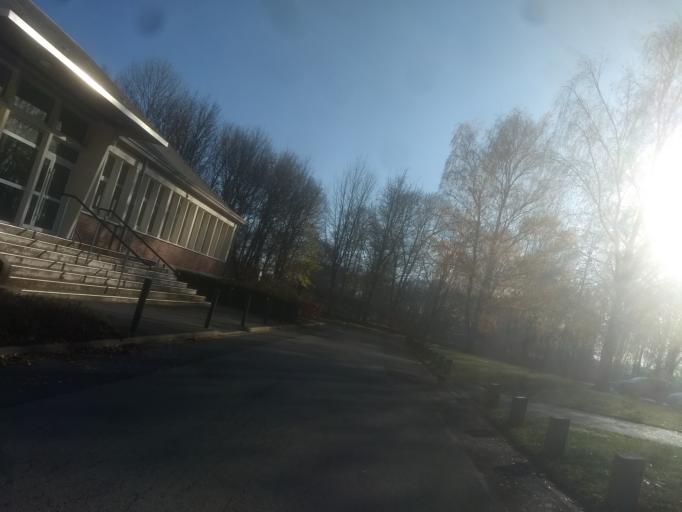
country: FR
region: Nord-Pas-de-Calais
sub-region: Departement du Pas-de-Calais
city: Achicourt
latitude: 50.2829
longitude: 2.7622
